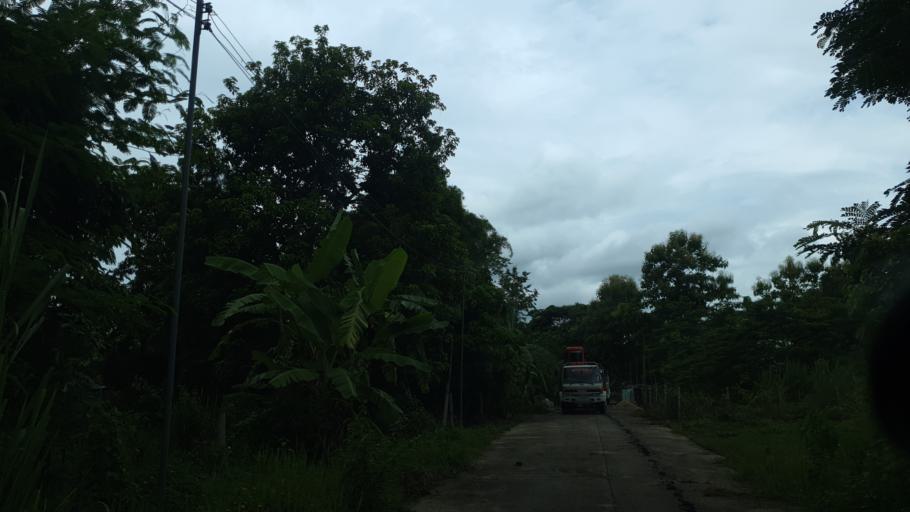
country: TH
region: Chiang Mai
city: San Kamphaeng
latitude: 18.7394
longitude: 99.1761
